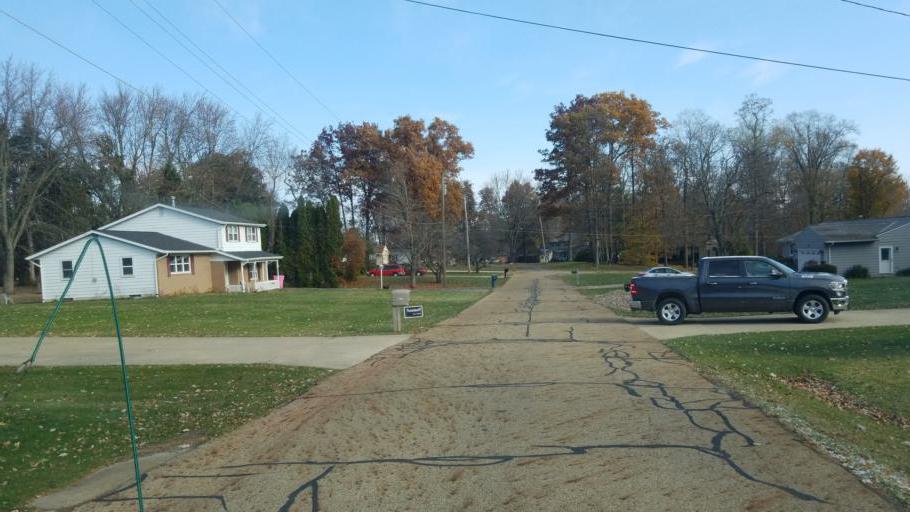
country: US
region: Ohio
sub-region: Richland County
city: Lexington
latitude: 40.7044
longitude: -82.5333
